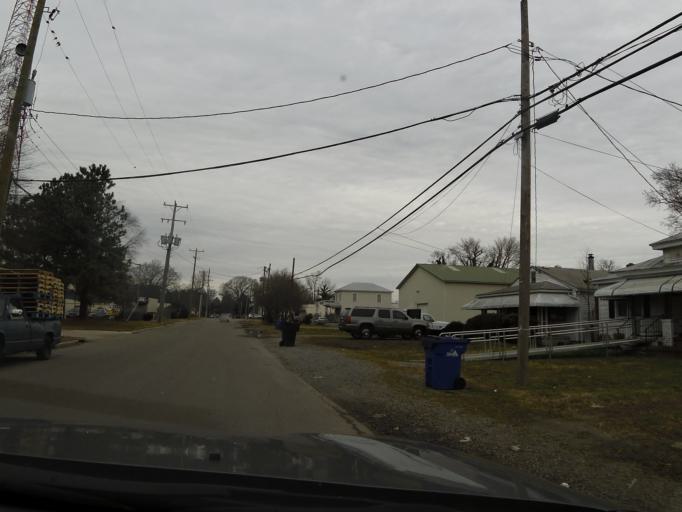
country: US
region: Virginia
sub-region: City of Portsmouth
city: Portsmouth
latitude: 36.8433
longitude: -76.3325
